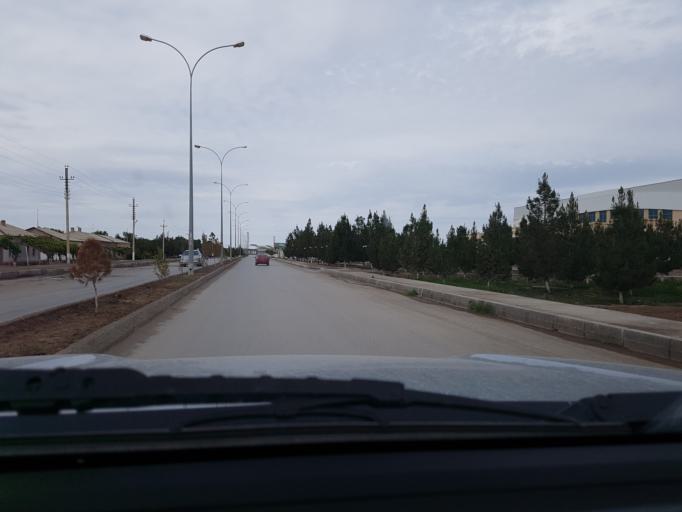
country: TM
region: Lebap
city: Sayat
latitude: 38.4862
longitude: 64.1463
